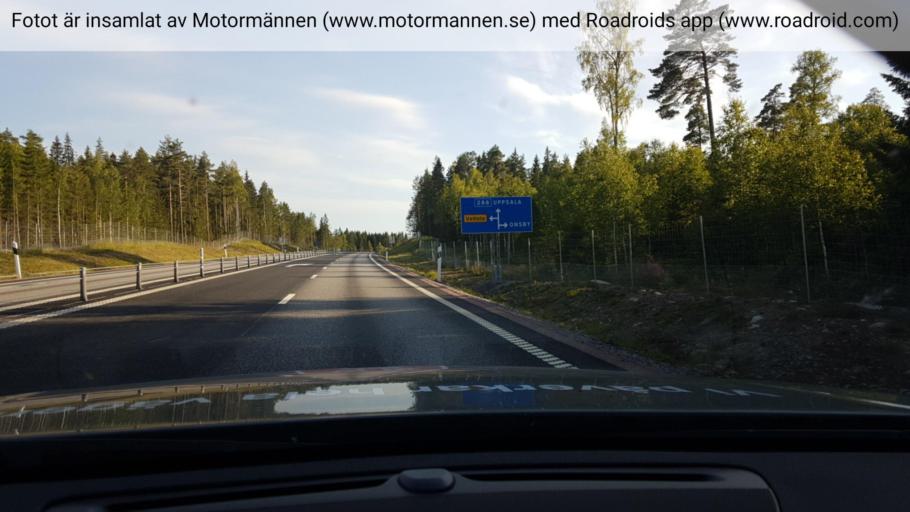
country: SE
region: Uppsala
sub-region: Osthammars Kommun
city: Gimo
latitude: 60.1280
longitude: 18.1531
